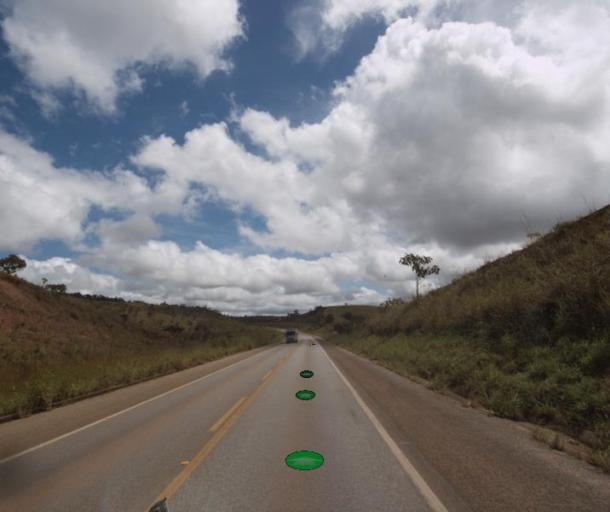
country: BR
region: Federal District
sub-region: Brasilia
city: Brasilia
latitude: -15.7536
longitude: -48.4228
